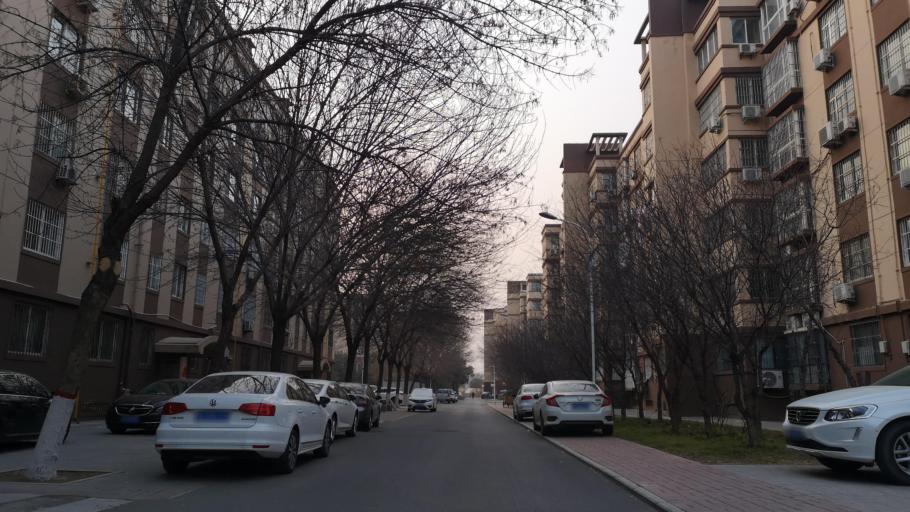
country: CN
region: Henan Sheng
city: Zhongyuanlu
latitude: 35.7888
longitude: 115.0775
